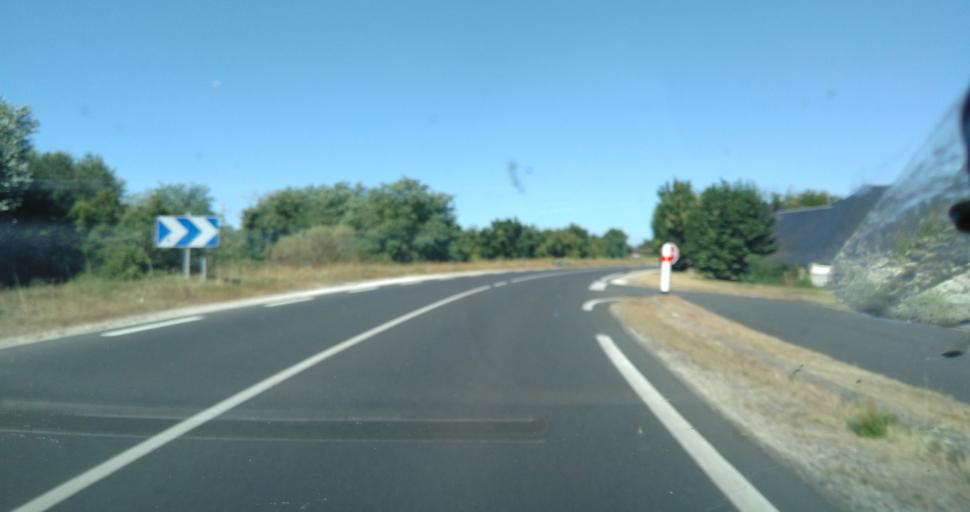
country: FR
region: Centre
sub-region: Departement d'Indre-et-Loire
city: Montlouis-sur-Loire
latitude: 47.3959
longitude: 0.8272
